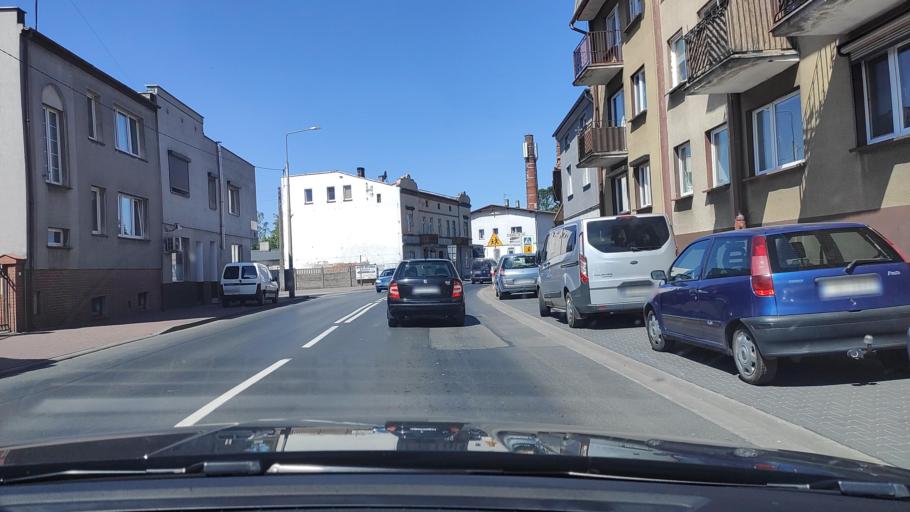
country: PL
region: Greater Poland Voivodeship
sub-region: Powiat obornicki
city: Rogozno
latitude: 52.7498
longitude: 17.0007
